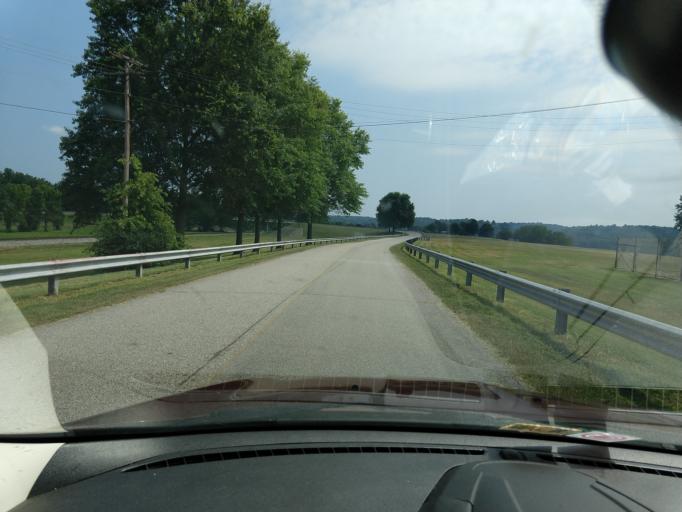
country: US
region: West Virginia
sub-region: Mason County
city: New Haven
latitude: 38.9197
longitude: -81.9128
